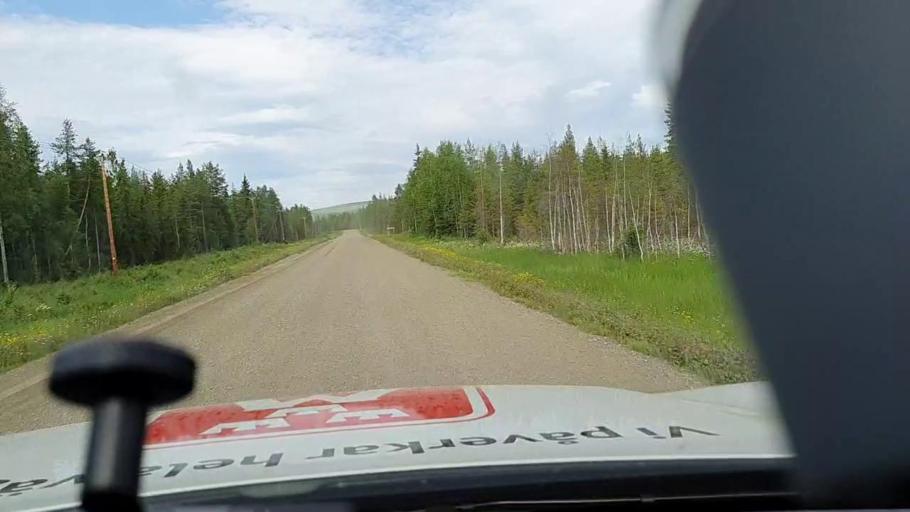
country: SE
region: Norrbotten
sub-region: Alvsbyns Kommun
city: AElvsbyn
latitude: 66.1393
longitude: 21.0080
